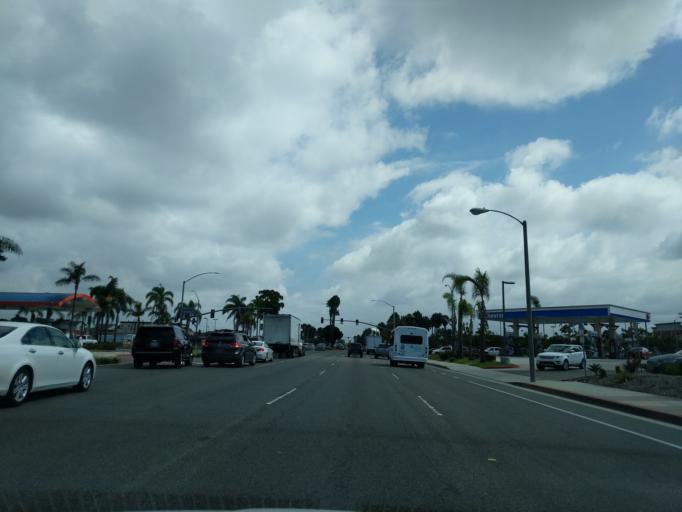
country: US
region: California
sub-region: Orange County
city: Midway City
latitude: 33.7155
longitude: -118.0077
